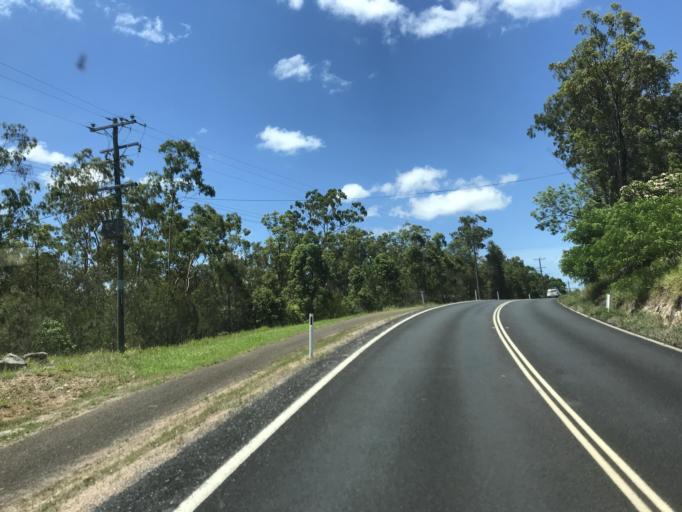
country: AU
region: Queensland
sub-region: Tablelands
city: Atherton
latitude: -17.3935
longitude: 145.3876
